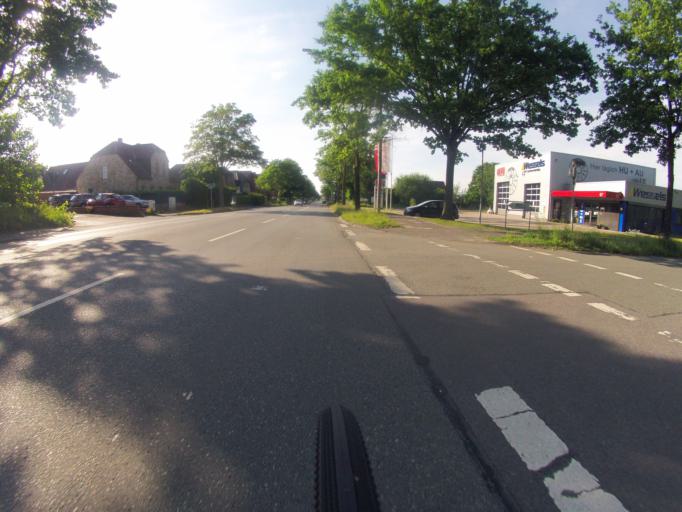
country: DE
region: North Rhine-Westphalia
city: Ibbenburen
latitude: 52.2616
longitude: 7.7235
